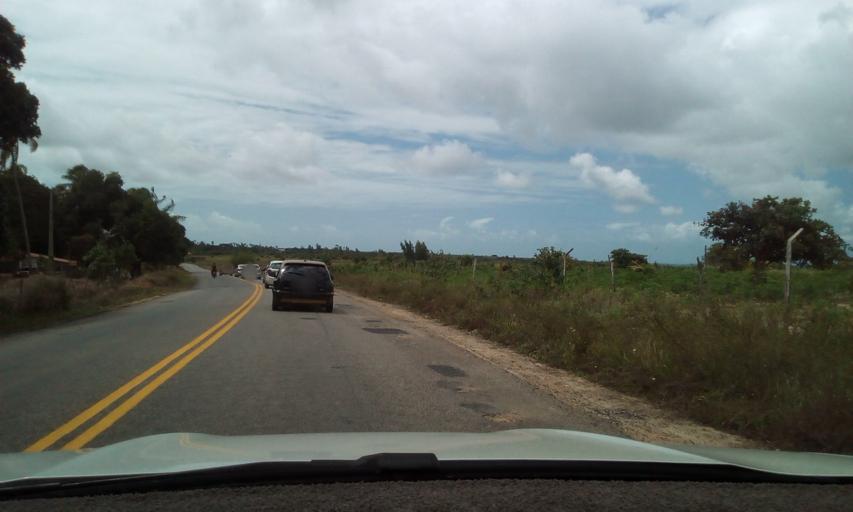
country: BR
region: Paraiba
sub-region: Rio Tinto
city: Rio Tinto
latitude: -6.7717
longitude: -35.0295
